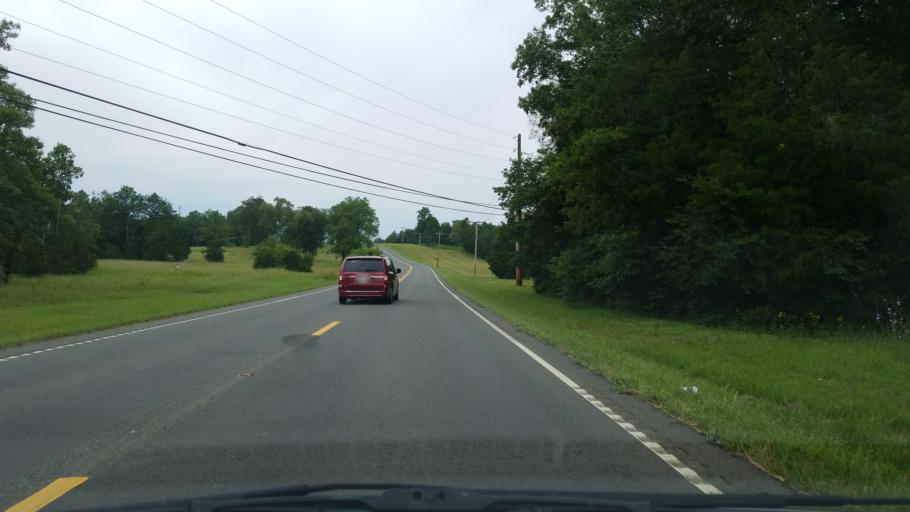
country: US
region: Tennessee
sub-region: Bradley County
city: Hopewell
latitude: 35.3135
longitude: -84.9502
